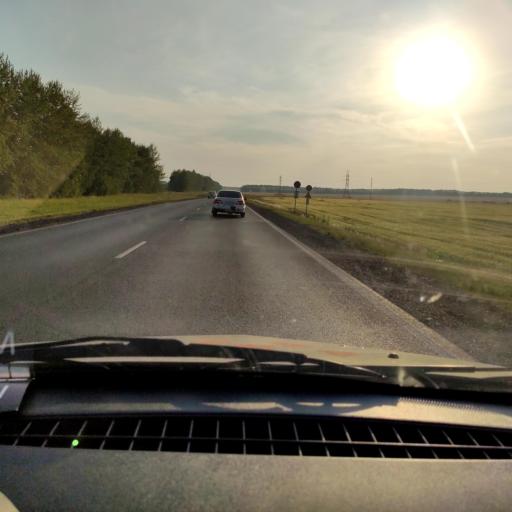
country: RU
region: Bashkortostan
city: Avdon
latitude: 54.5814
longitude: 55.7745
